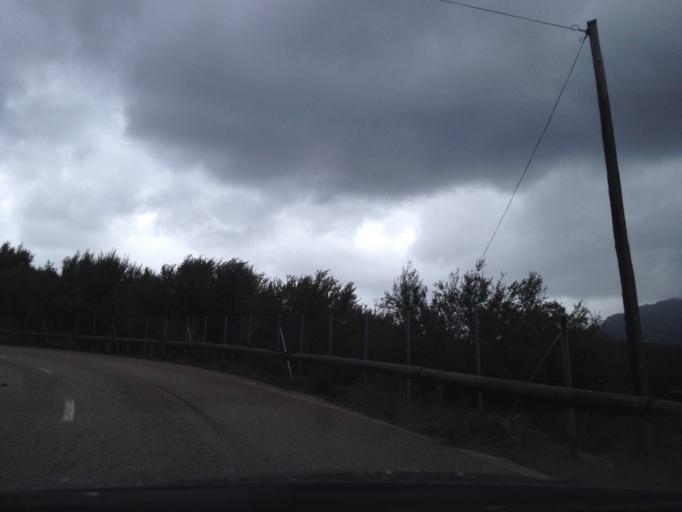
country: ES
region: Balearic Islands
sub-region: Illes Balears
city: Soller
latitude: 39.7750
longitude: 2.6960
